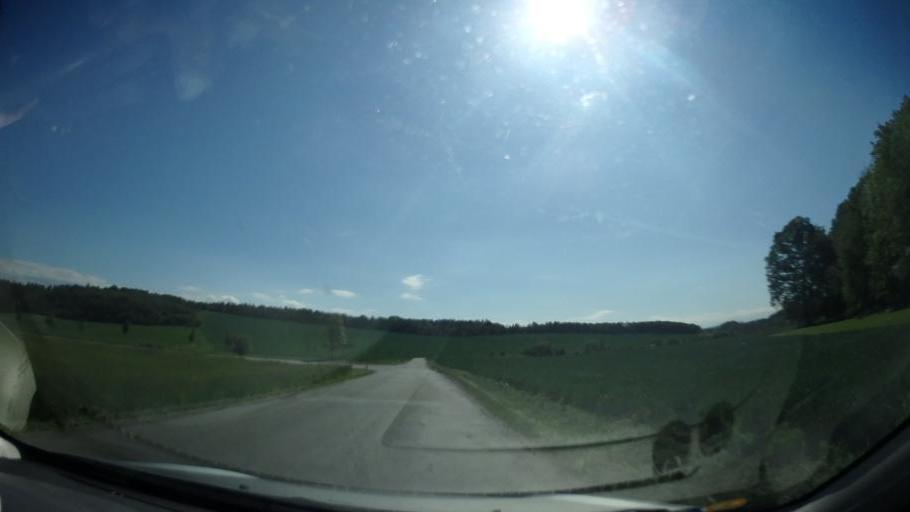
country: CZ
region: South Moravian
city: Velke Opatovice
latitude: 49.6235
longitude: 16.6114
